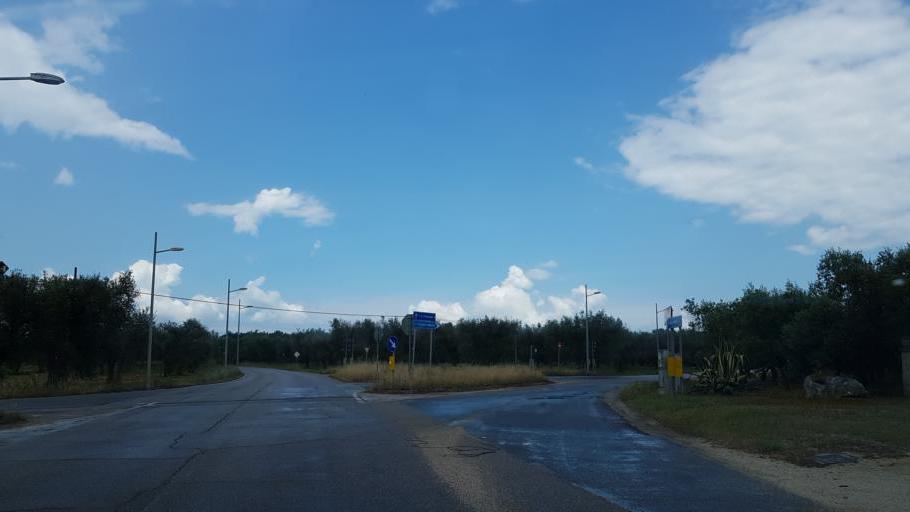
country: IT
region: Apulia
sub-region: Provincia di Brindisi
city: Cellino San Marco
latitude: 40.4741
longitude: 17.9358
